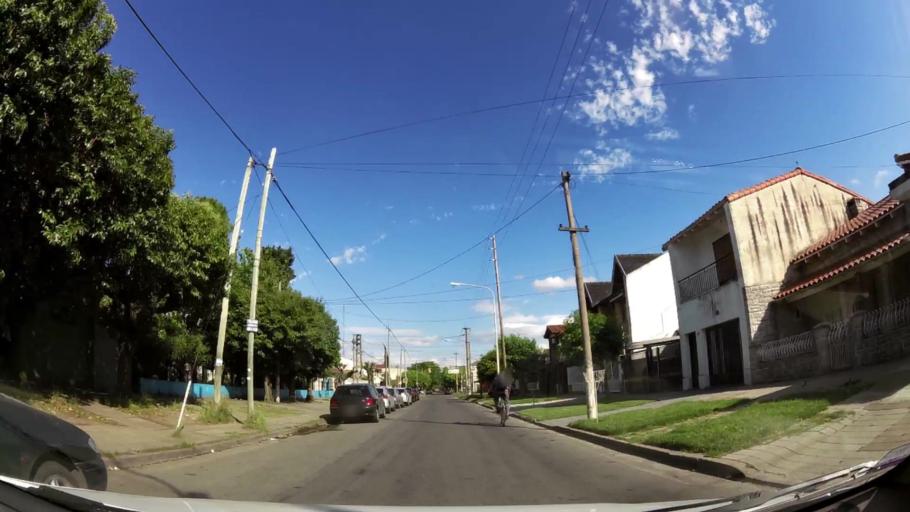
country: AR
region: Buenos Aires
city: San Justo
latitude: -34.6667
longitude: -58.5857
